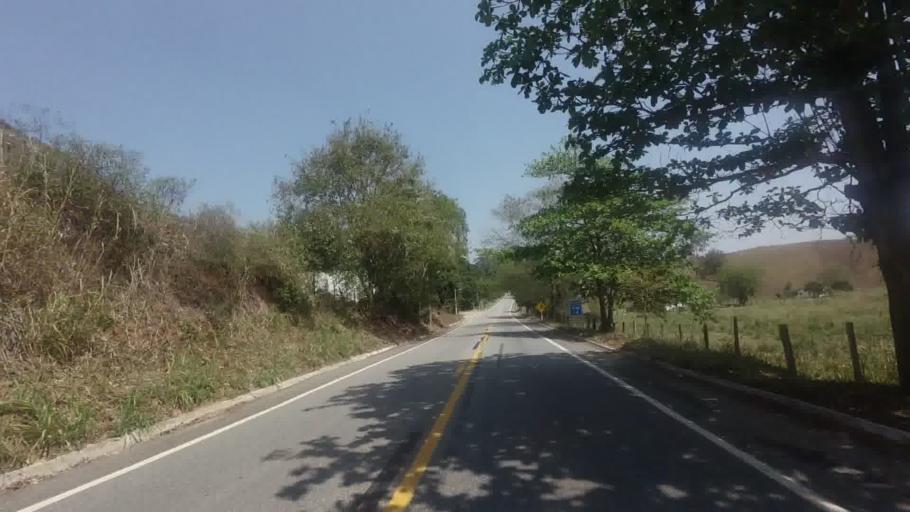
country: BR
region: Espirito Santo
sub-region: Cachoeiro De Itapemirim
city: Cachoeiro de Itapemirim
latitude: -20.8624
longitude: -41.2536
